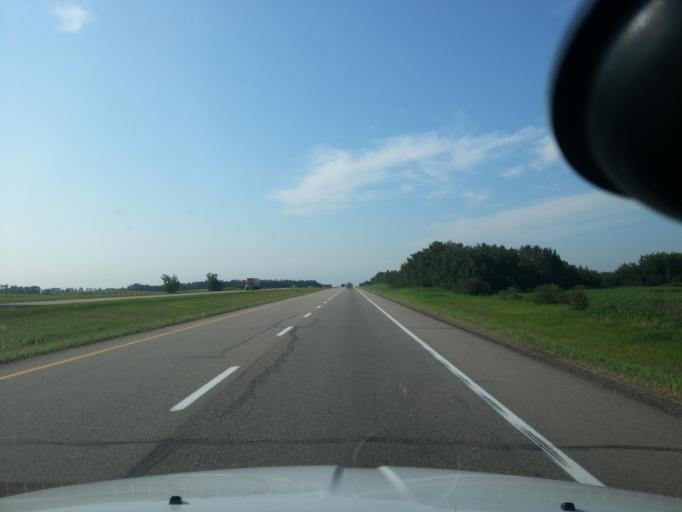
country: CA
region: Alberta
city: Ponoka
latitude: 52.7264
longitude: -113.6441
